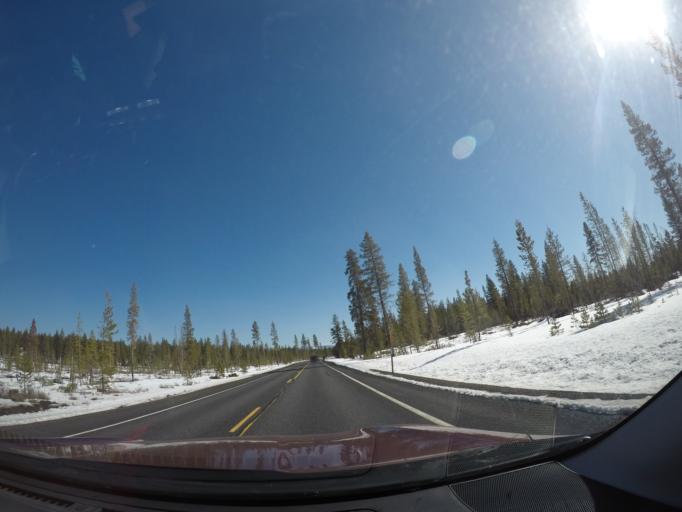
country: US
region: Oregon
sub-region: Deschutes County
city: Three Rivers
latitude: 43.8631
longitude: -121.5336
